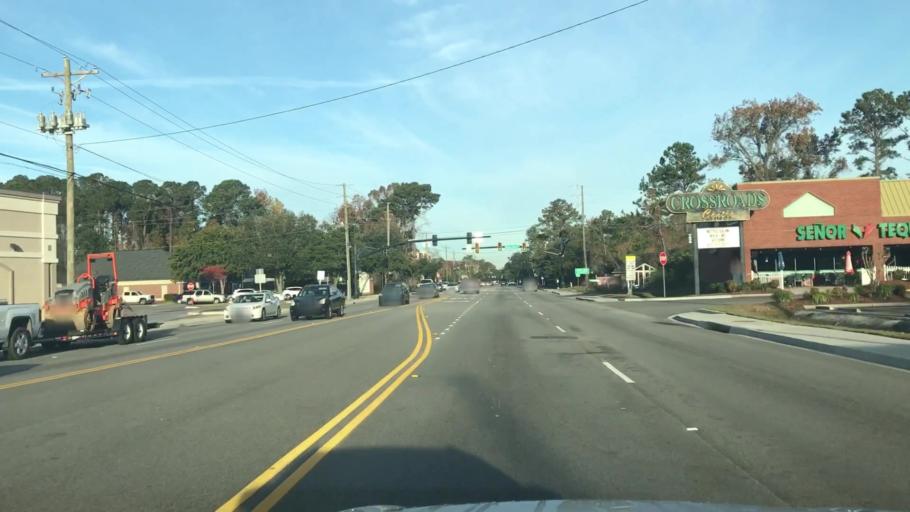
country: US
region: South Carolina
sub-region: Charleston County
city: North Charleston
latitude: 32.8031
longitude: -80.0184
